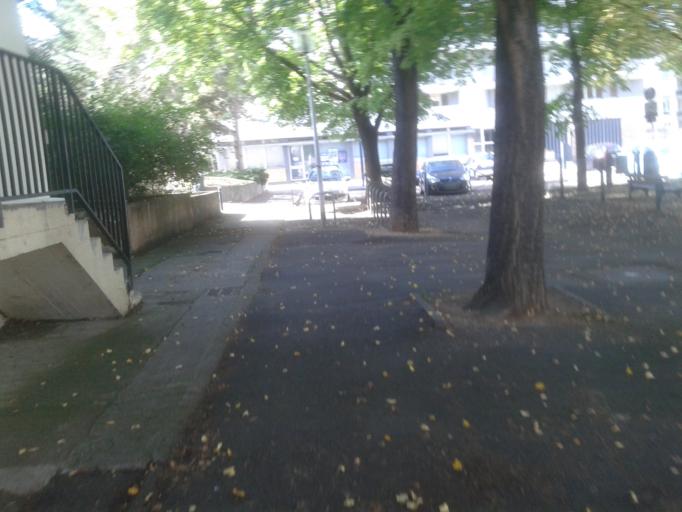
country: FR
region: Auvergne
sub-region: Departement du Puy-de-Dome
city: Clermont-Ferrand
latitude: 45.7713
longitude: 3.0770
